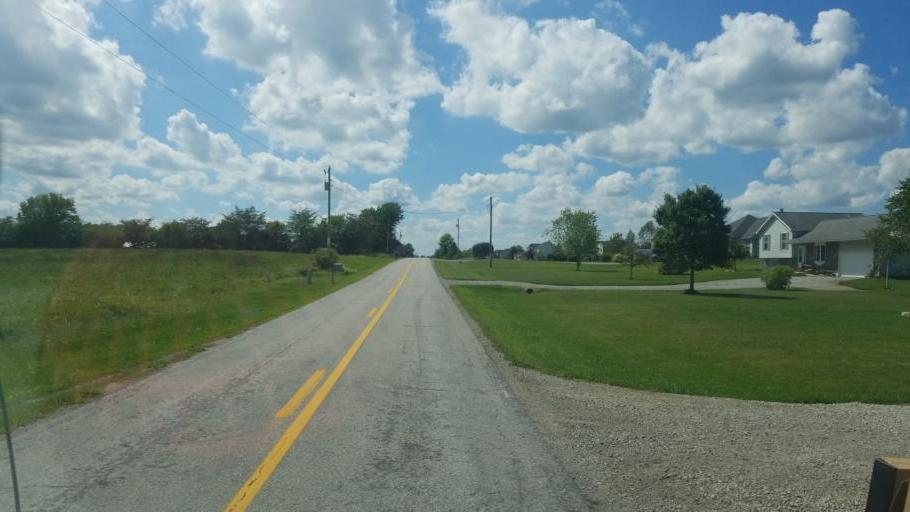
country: US
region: Ohio
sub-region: Marion County
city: Prospect
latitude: 40.3497
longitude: -83.1853
